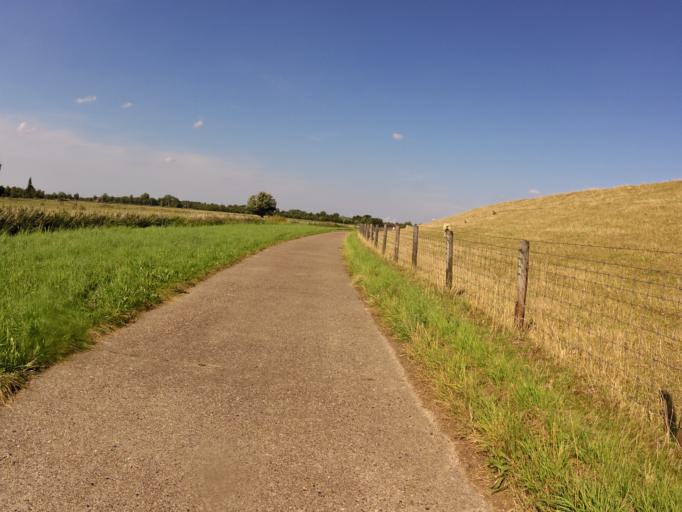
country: DE
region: Lower Saxony
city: Ovelgonne
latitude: 53.3866
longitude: 8.4583
